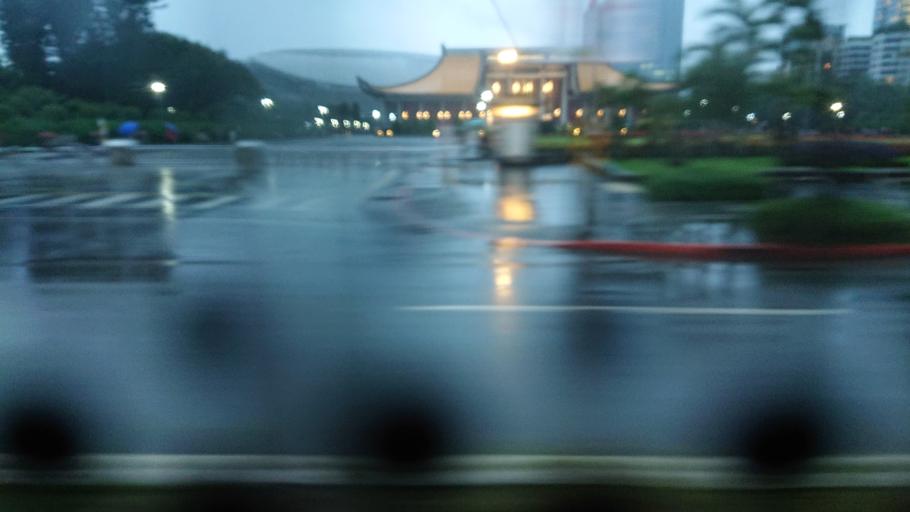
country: TW
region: Taipei
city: Taipei
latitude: 25.0377
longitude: 121.5600
